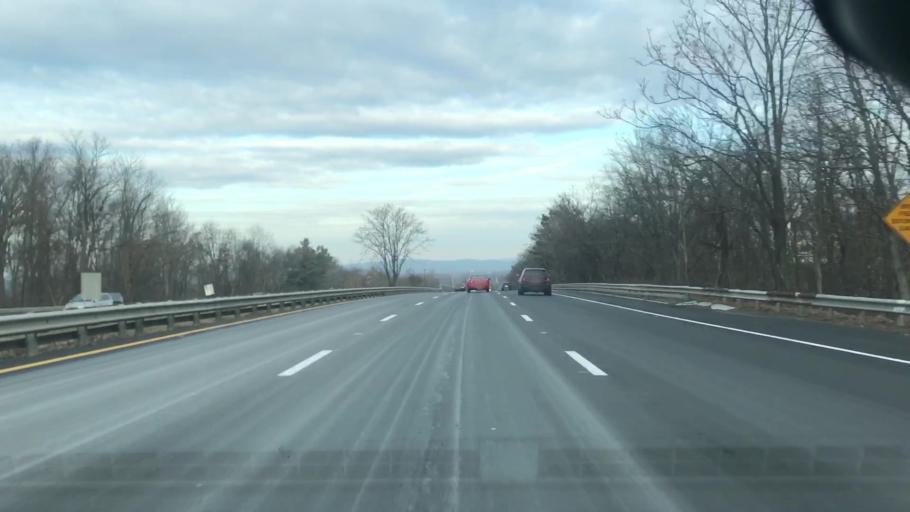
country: US
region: New Jersey
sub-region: Essex County
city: Roseland
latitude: 40.8176
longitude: -74.3141
